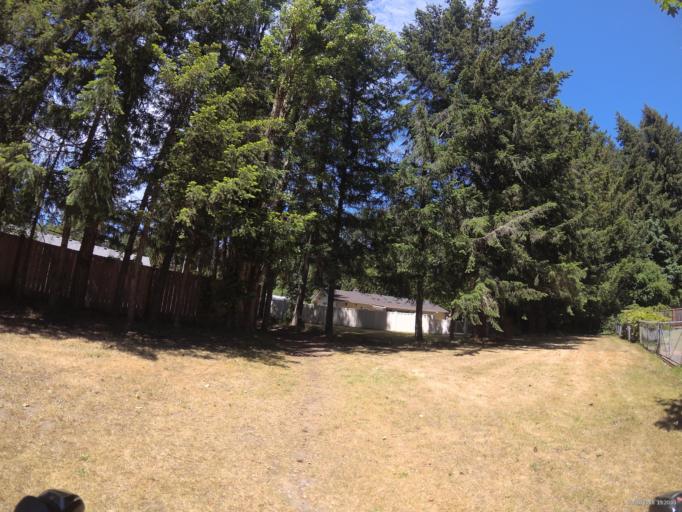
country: US
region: Washington
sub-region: Pierce County
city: University Place
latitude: 47.2089
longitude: -122.5599
